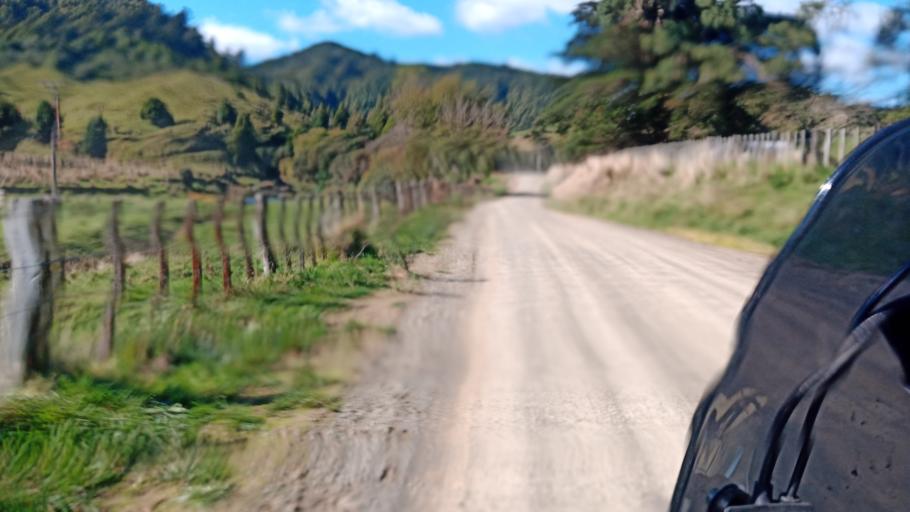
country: NZ
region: Bay of Plenty
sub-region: Opotiki District
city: Opotiki
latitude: -38.2513
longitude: 177.5844
